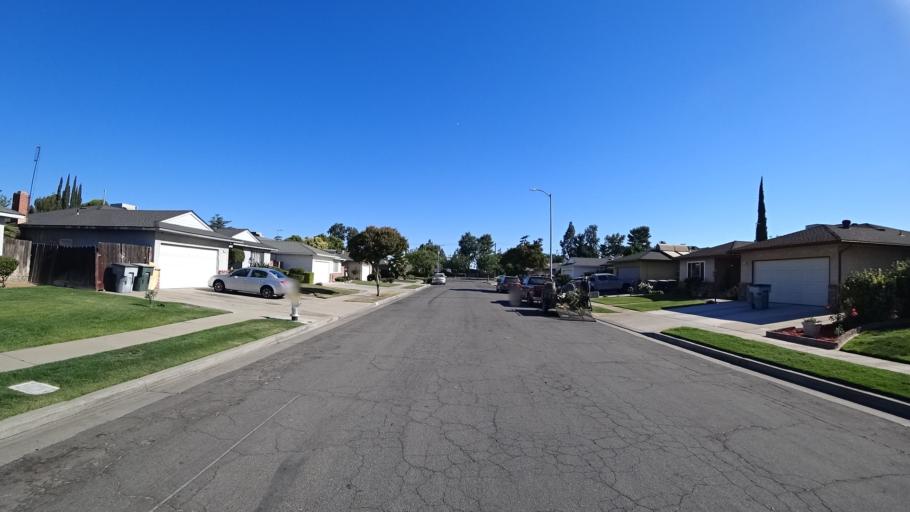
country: US
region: California
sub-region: Fresno County
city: Fresno
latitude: 36.7925
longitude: -119.8412
